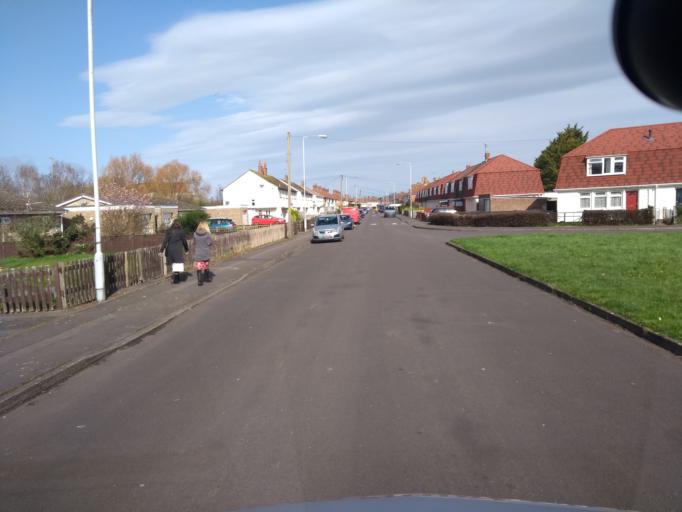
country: GB
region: England
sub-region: Somerset
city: Bridgwater
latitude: 51.1325
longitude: -2.9855
